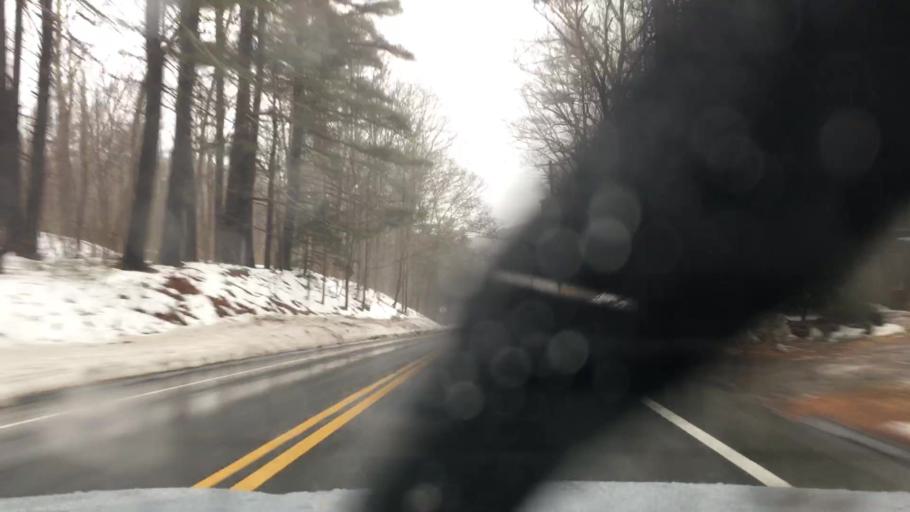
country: US
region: Massachusetts
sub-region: Franklin County
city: Shutesbury
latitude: 42.4882
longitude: -72.3412
